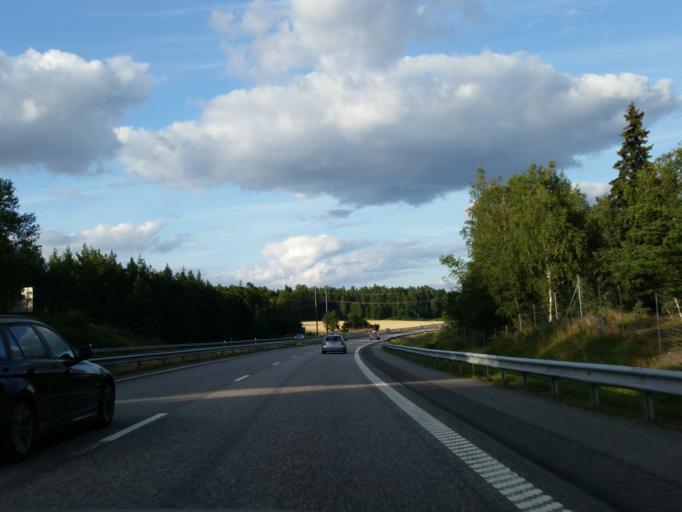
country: SE
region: Stockholm
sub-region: Sodertalje Kommun
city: Pershagen
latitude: 59.1155
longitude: 17.6144
